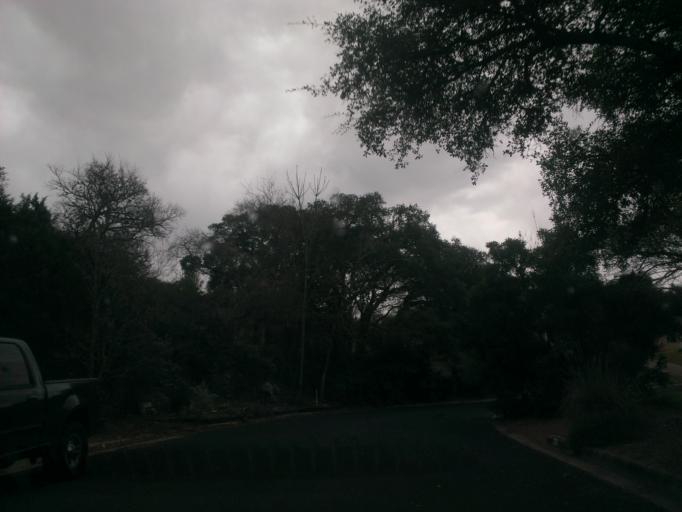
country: US
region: Texas
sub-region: Williamson County
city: Jollyville
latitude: 30.3701
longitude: -97.7685
